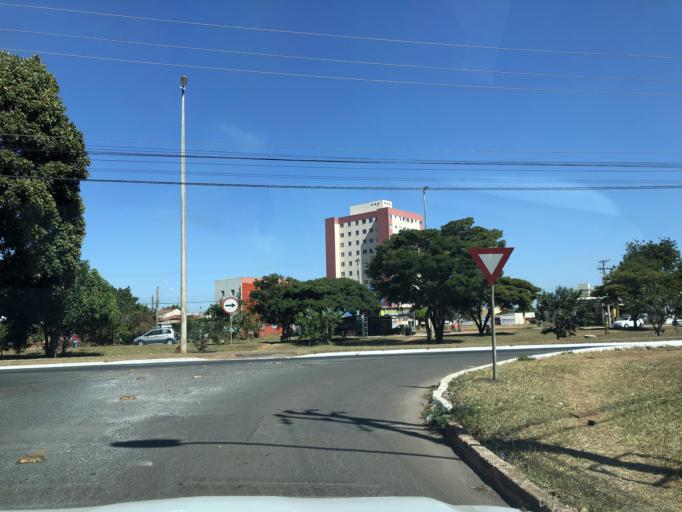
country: BR
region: Federal District
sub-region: Brasilia
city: Brasilia
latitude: -15.8760
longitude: -48.0616
